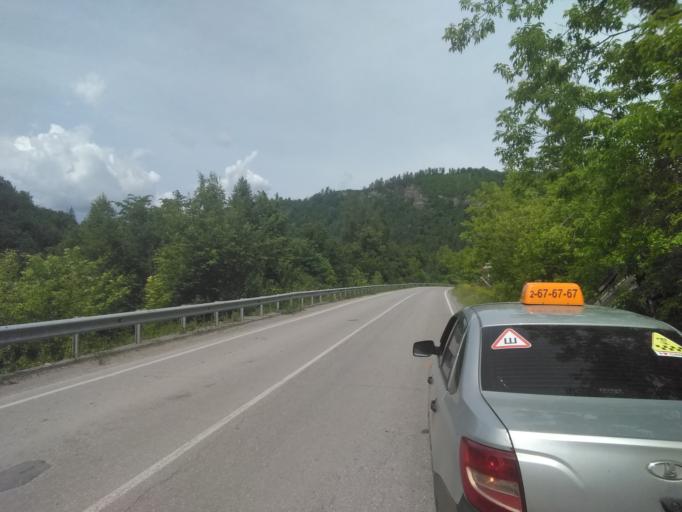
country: RU
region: Chelyabinsk
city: Sim
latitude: 55.0648
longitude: 57.6037
